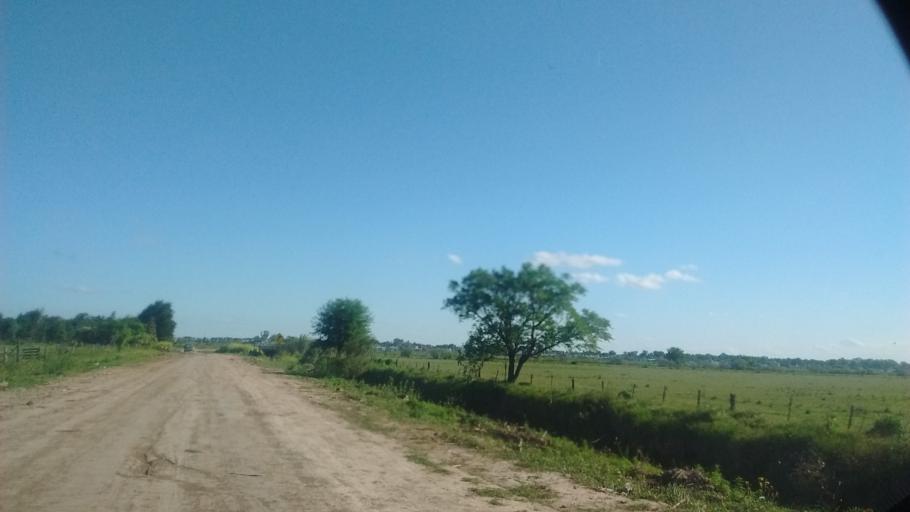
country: AR
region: Santa Fe
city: Funes
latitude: -32.8918
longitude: -60.7978
